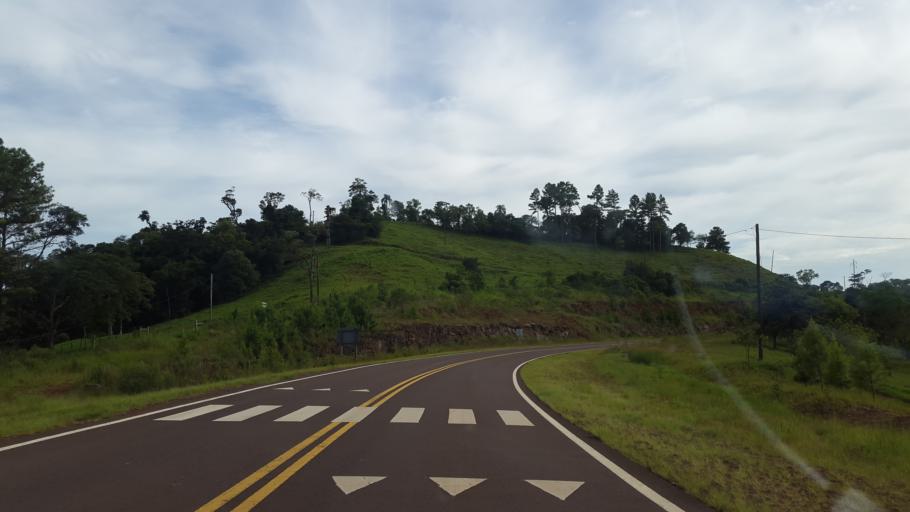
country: AR
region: Misiones
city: Bernardo de Irigoyen
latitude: -26.3975
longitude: -53.8162
